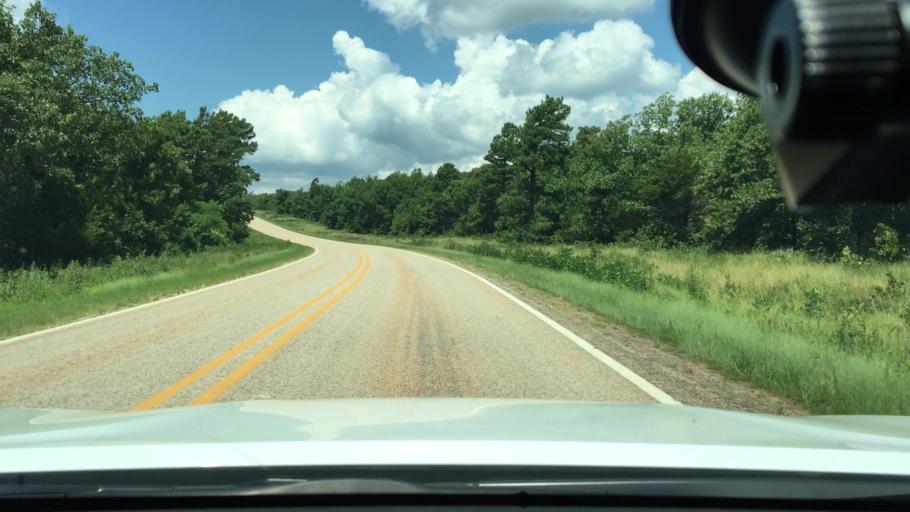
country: US
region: Arkansas
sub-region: Logan County
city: Paris
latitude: 35.1771
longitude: -93.6026
